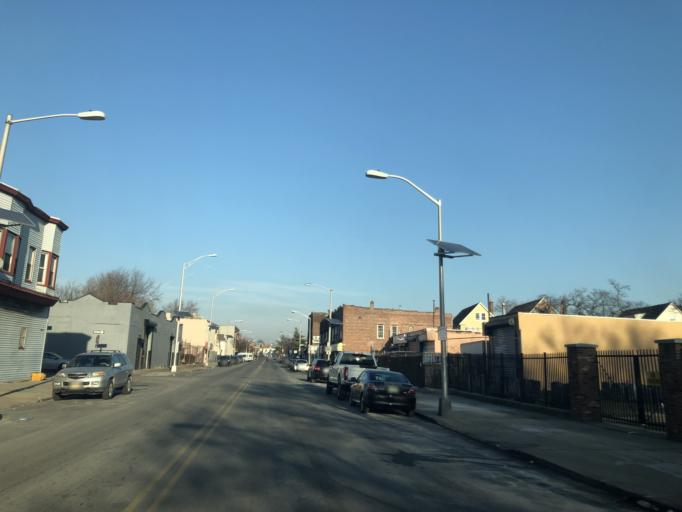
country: US
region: New Jersey
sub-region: Hudson County
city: Jersey City
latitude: 40.6984
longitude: -74.0863
